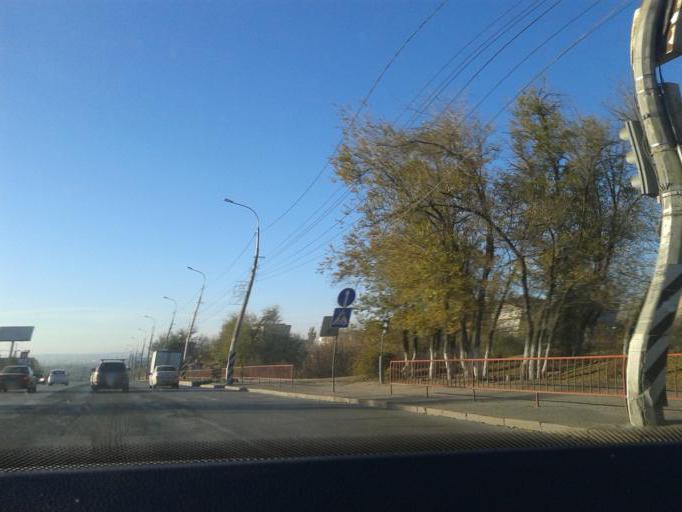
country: RU
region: Volgograd
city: Volgograd
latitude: 48.6709
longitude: 44.4423
